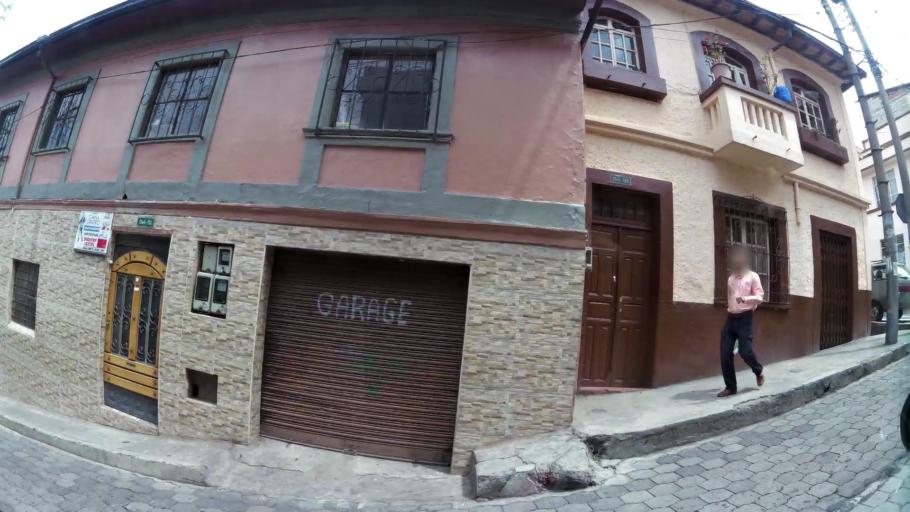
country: EC
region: Pichincha
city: Quito
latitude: -0.2136
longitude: -78.5097
